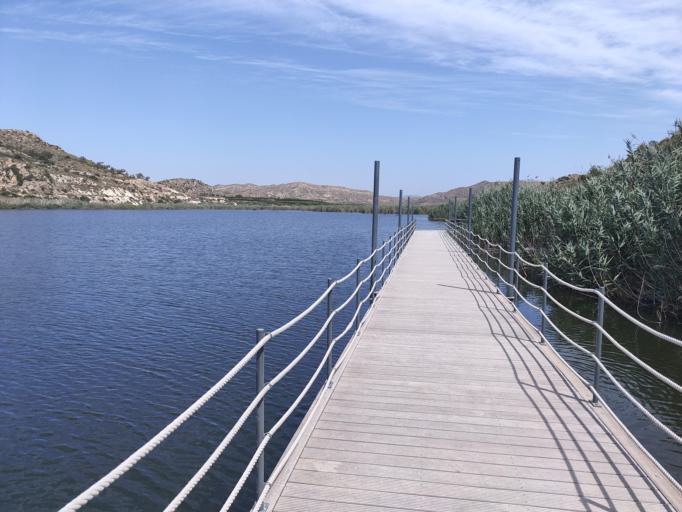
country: ES
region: Valencia
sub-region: Provincia de Alicante
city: Elche
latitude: 38.3077
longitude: -0.7209
